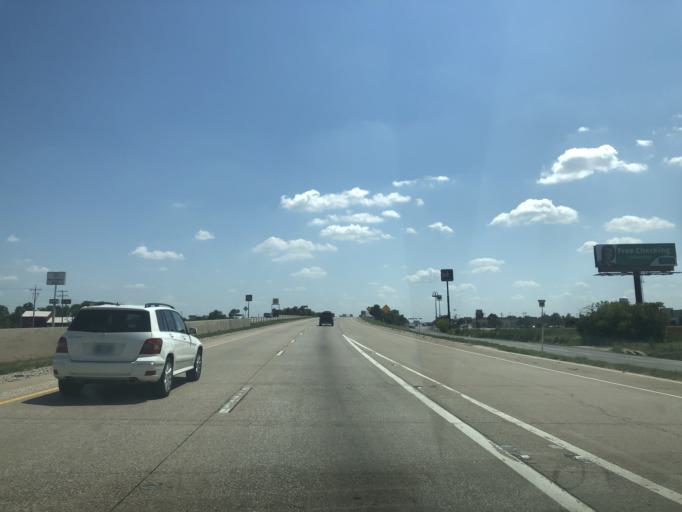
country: US
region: Texas
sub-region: Denton County
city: Sanger
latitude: 33.3702
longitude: -97.1780
